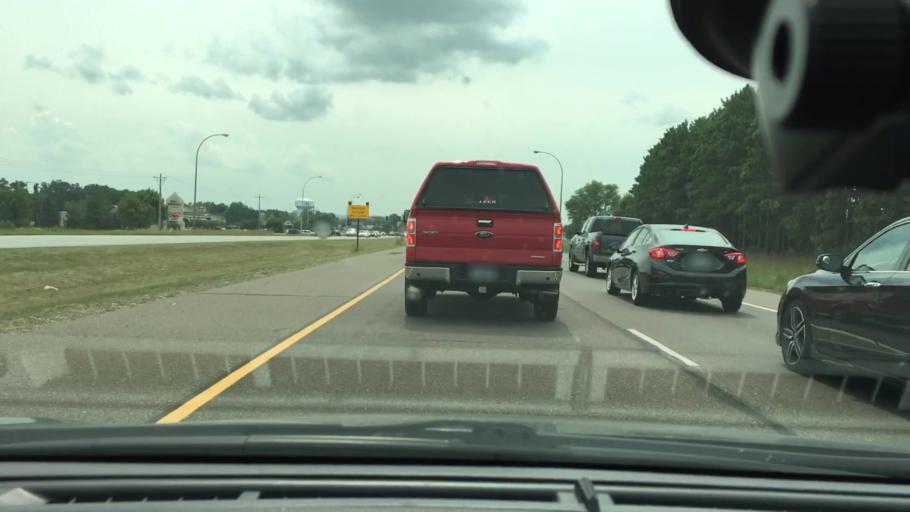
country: US
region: Minnesota
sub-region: Sherburne County
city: Elk River
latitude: 45.3241
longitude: -93.5618
